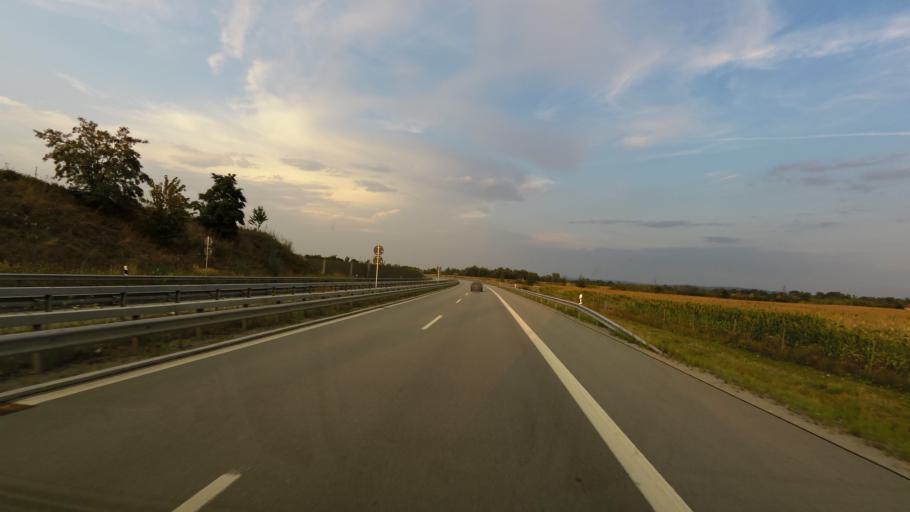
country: DE
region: Bavaria
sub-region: Lower Bavaria
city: Malching
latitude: 48.3062
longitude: 13.1783
